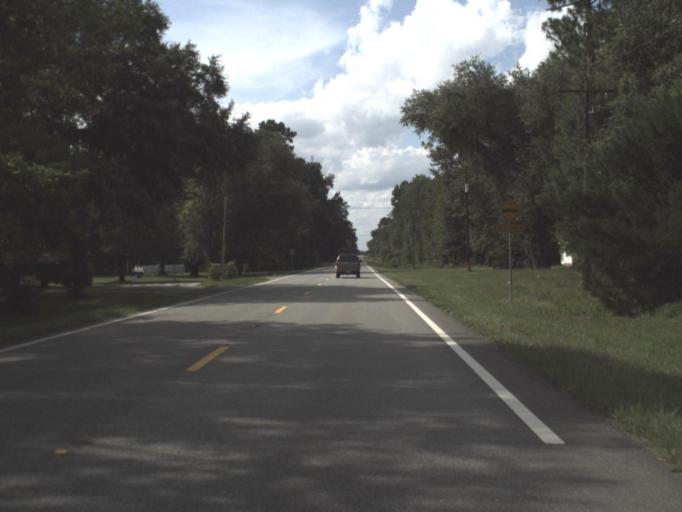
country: US
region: Florida
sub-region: Taylor County
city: Perry
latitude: 30.3513
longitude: -83.6511
